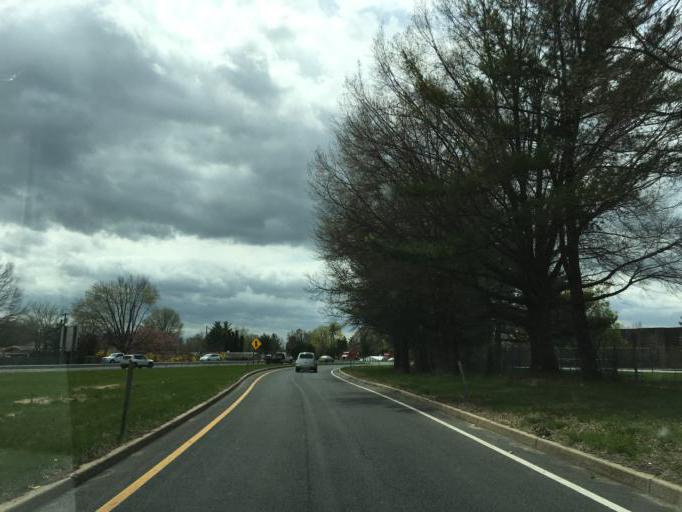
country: US
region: Maryland
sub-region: Frederick County
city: Frederick
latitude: 39.4349
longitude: -77.4124
